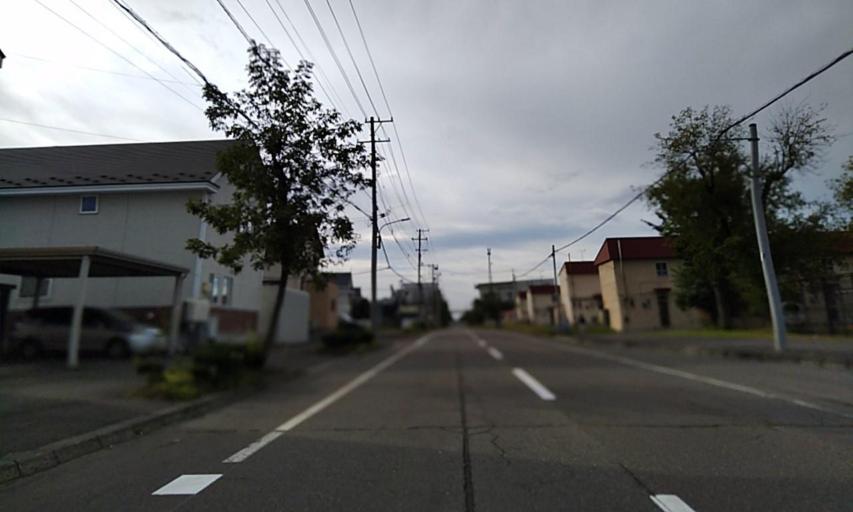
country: JP
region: Hokkaido
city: Obihiro
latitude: 42.9135
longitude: 143.0427
